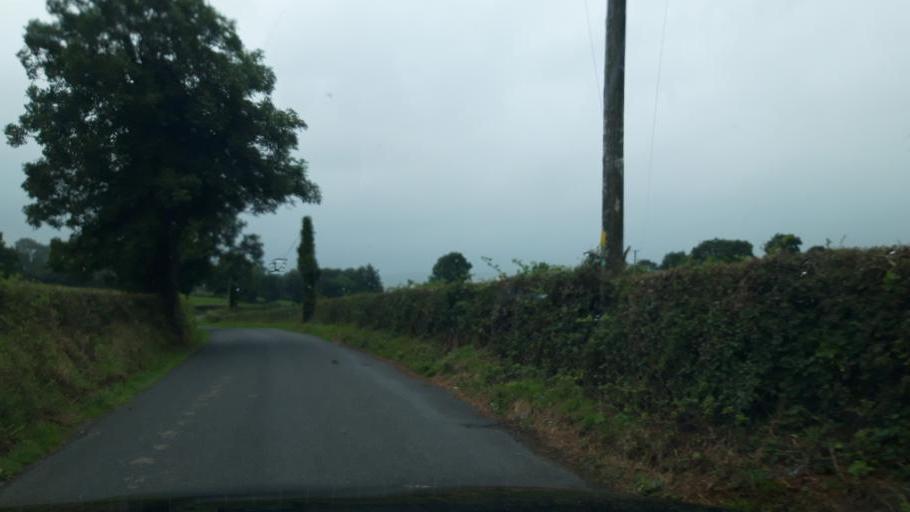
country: IE
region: Leinster
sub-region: Kilkenny
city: Ballyragget
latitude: 52.6866
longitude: -7.4298
